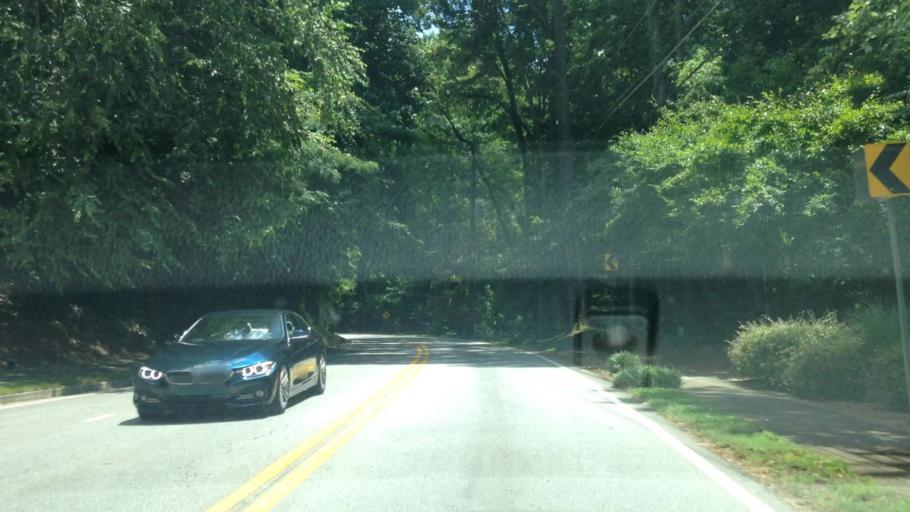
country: US
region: Georgia
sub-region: DeKalb County
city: North Atlanta
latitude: 33.8832
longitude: -84.3537
